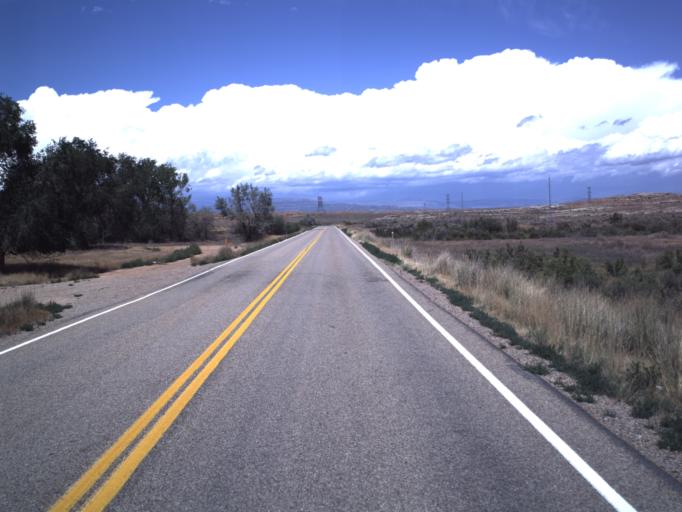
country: US
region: Utah
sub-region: Uintah County
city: Maeser
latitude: 40.2549
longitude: -109.6844
